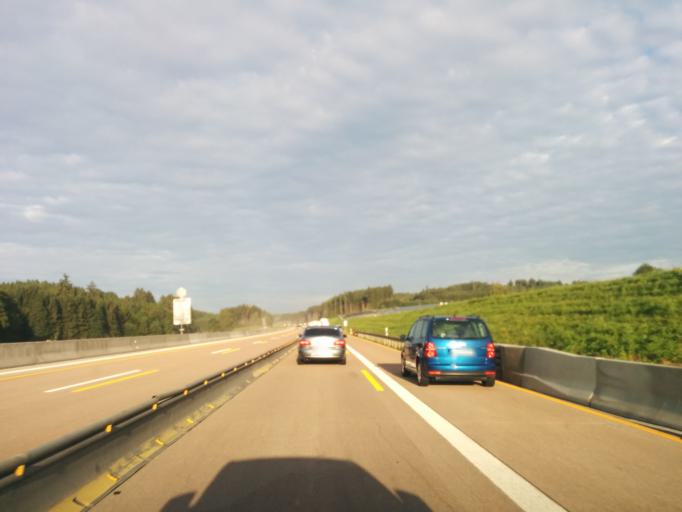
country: DE
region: Bavaria
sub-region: Swabia
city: Aystetten
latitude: 48.4203
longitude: 10.8008
